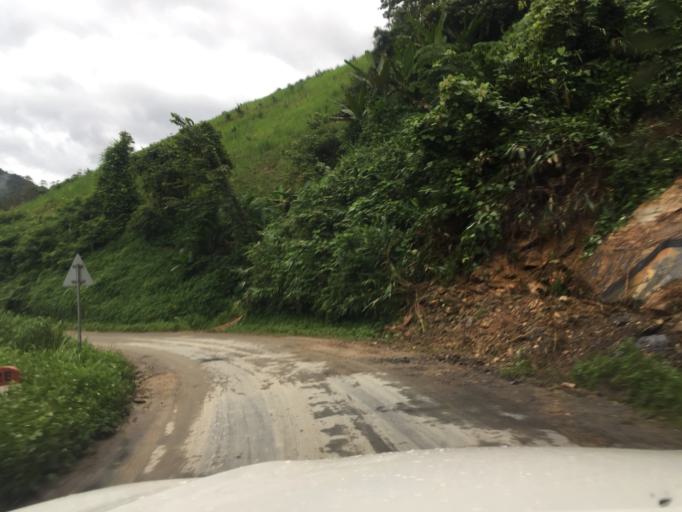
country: LA
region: Oudomxai
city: Muang La
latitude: 21.0037
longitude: 102.2323
